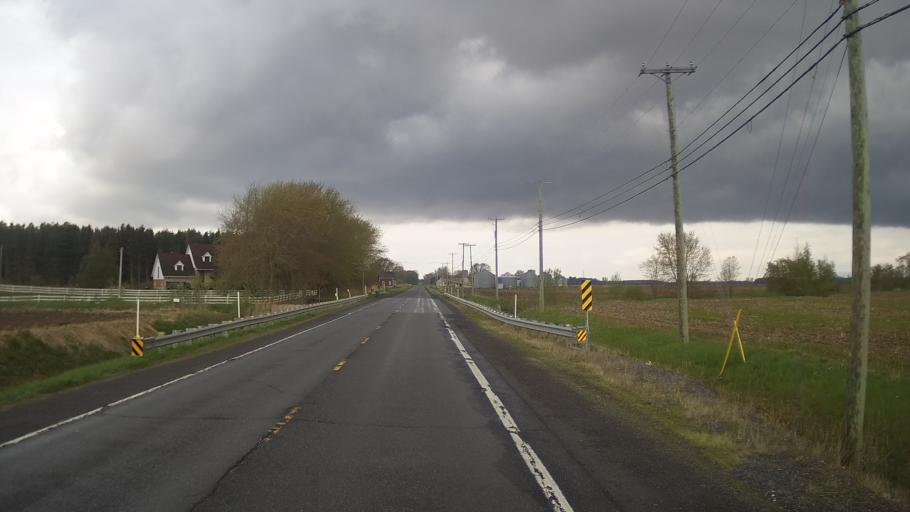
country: CA
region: Quebec
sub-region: Monteregie
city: Rougemont
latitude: 45.3317
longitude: -73.0771
